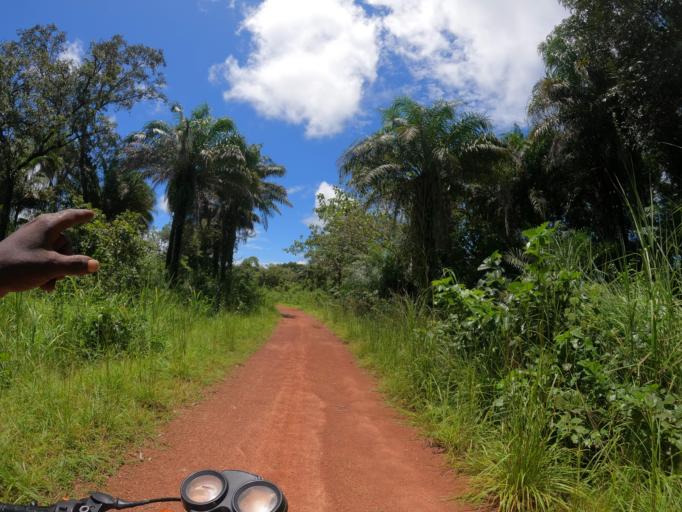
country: SL
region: Northern Province
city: Makeni
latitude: 9.0853
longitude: -12.2678
